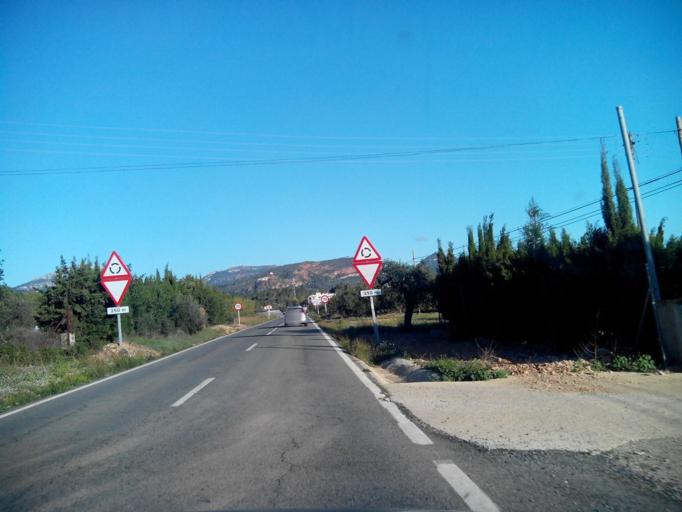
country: ES
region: Catalonia
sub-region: Provincia de Tarragona
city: Vilanova d'Escornalbou
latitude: 41.0795
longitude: 0.9648
